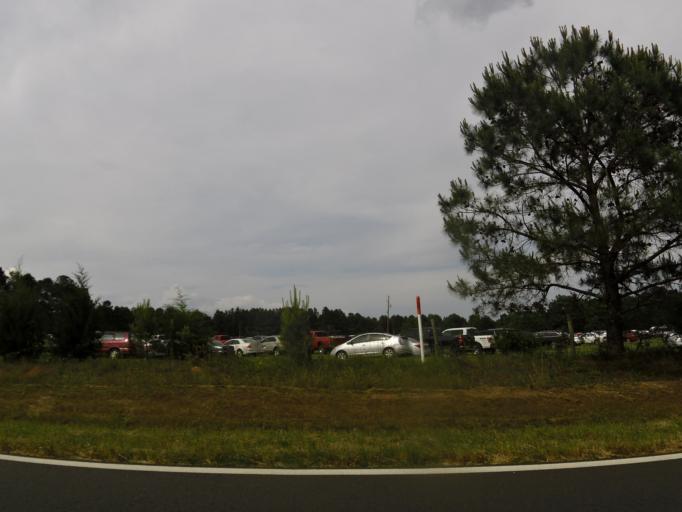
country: US
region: Georgia
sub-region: McDuffie County
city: Thomson
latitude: 33.5386
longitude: -82.5004
